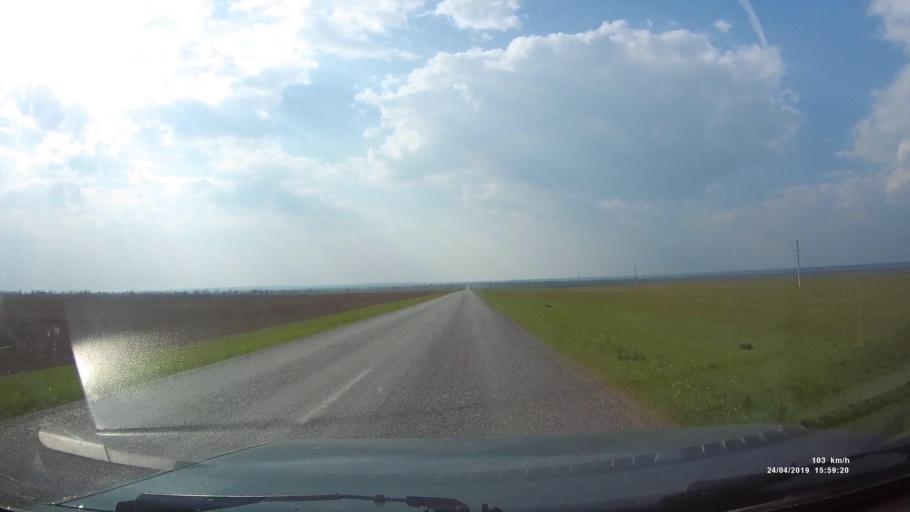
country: RU
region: Rostov
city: Sovetskoye
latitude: 46.6225
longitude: 42.4739
